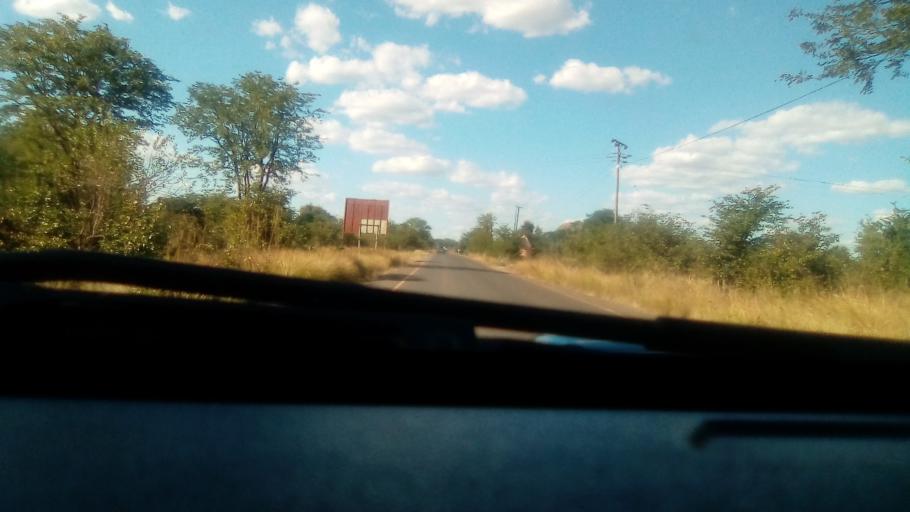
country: ZM
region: Southern
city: Livingstone
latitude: -17.8812
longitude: 25.8465
